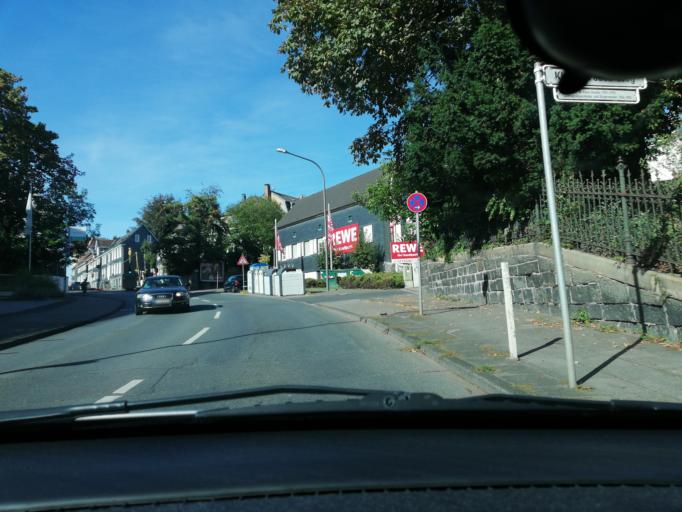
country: DE
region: North Rhine-Westphalia
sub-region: Regierungsbezirk Dusseldorf
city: Wuppertal
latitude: 51.2858
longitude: 7.2245
